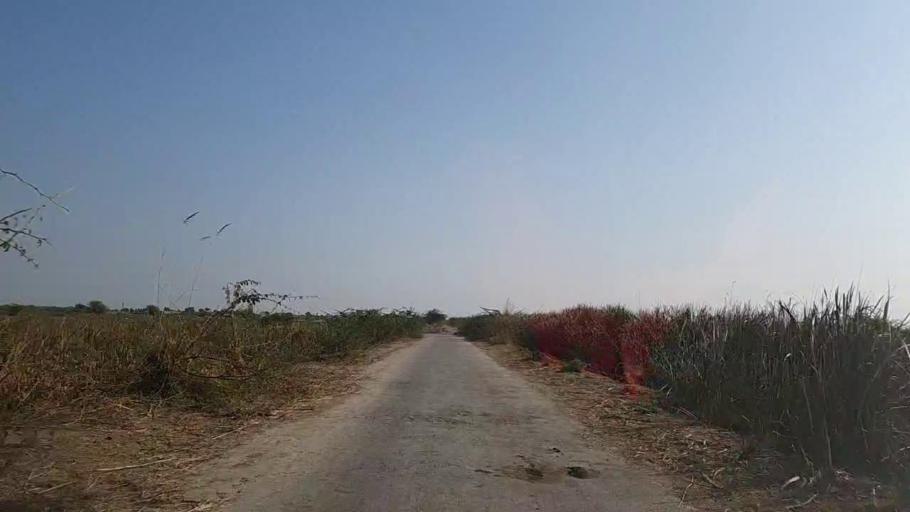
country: PK
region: Sindh
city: Sanghar
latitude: 25.9372
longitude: 69.0572
